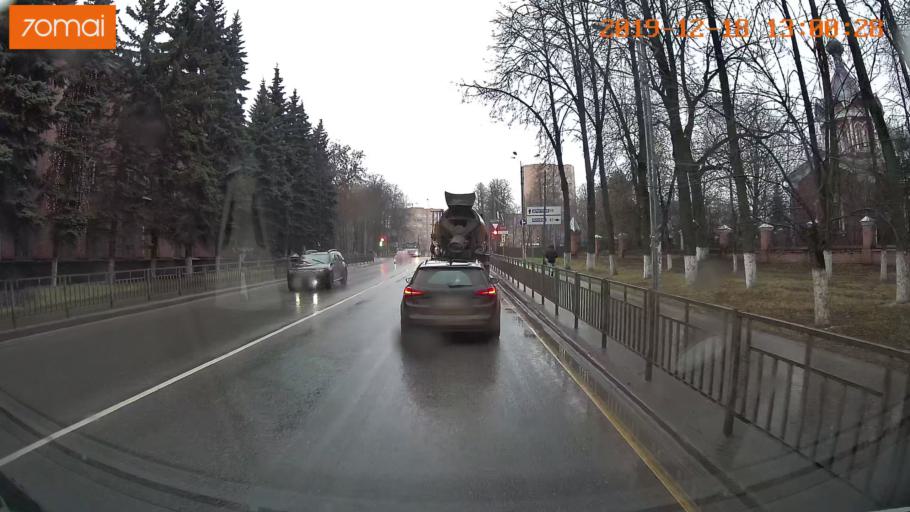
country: RU
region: Moskovskaya
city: Klin
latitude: 56.3318
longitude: 36.7256
